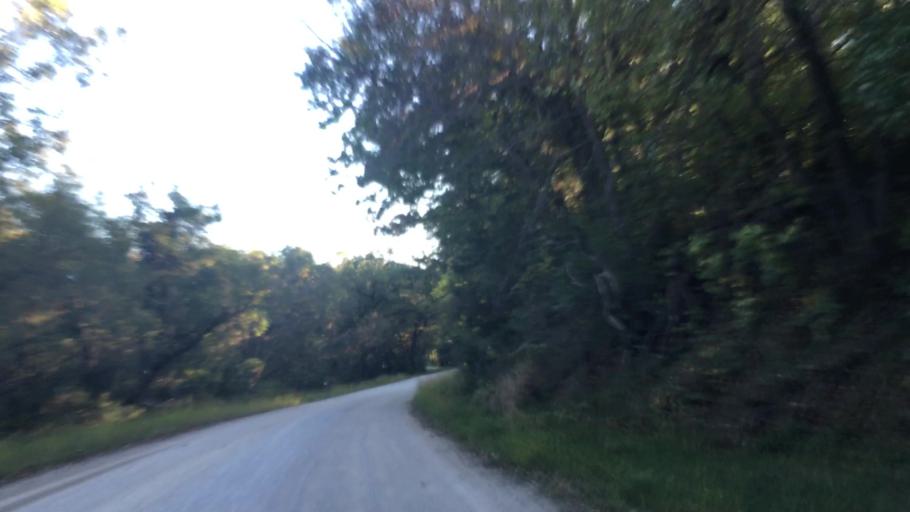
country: US
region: Minnesota
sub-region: Fillmore County
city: Preston
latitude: 43.7918
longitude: -92.0392
